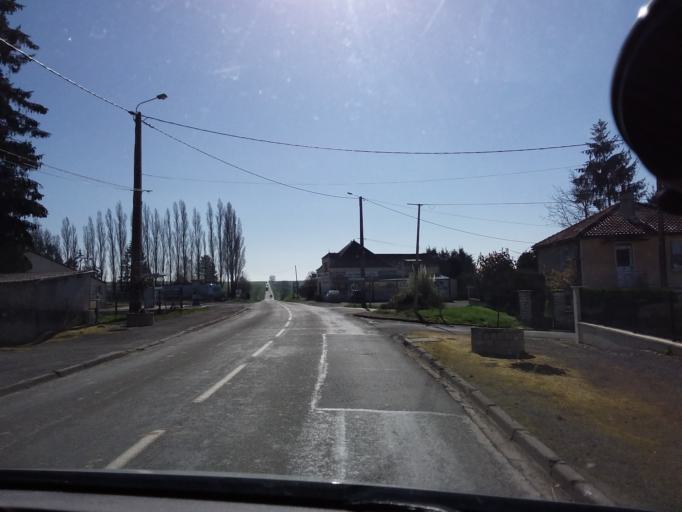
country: FR
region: Picardie
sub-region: Departement de l'Aisne
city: Montcornet
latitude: 49.6249
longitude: 4.0231
